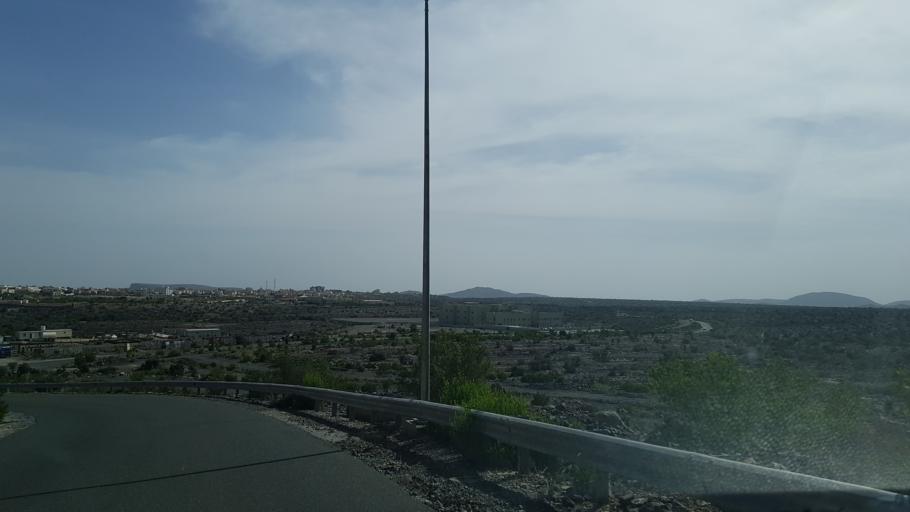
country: OM
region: Muhafazat ad Dakhiliyah
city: Izki
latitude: 23.0918
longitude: 57.6823
